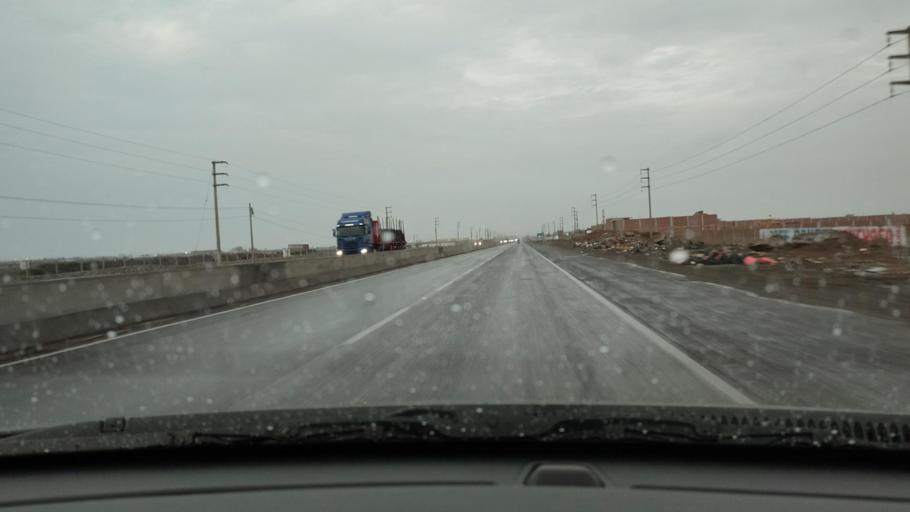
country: PE
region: La Libertad
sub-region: Provincia de Trujillo
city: Huanchaco
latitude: -8.0511
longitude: -79.0870
